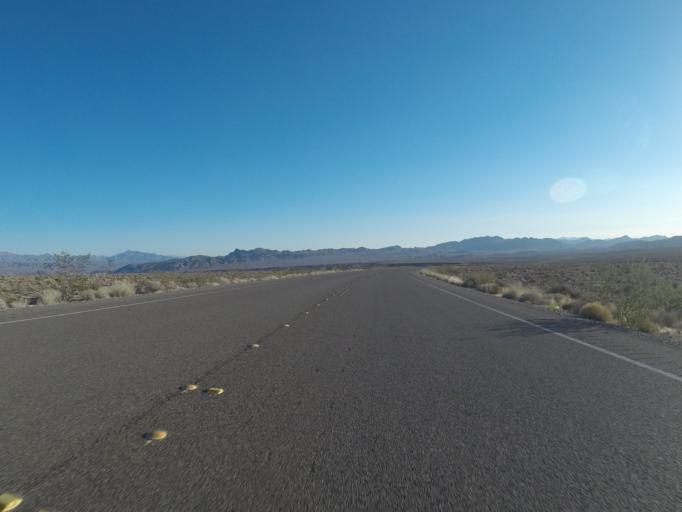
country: US
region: Nevada
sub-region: Clark County
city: Moapa Valley
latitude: 36.3556
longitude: -114.4827
